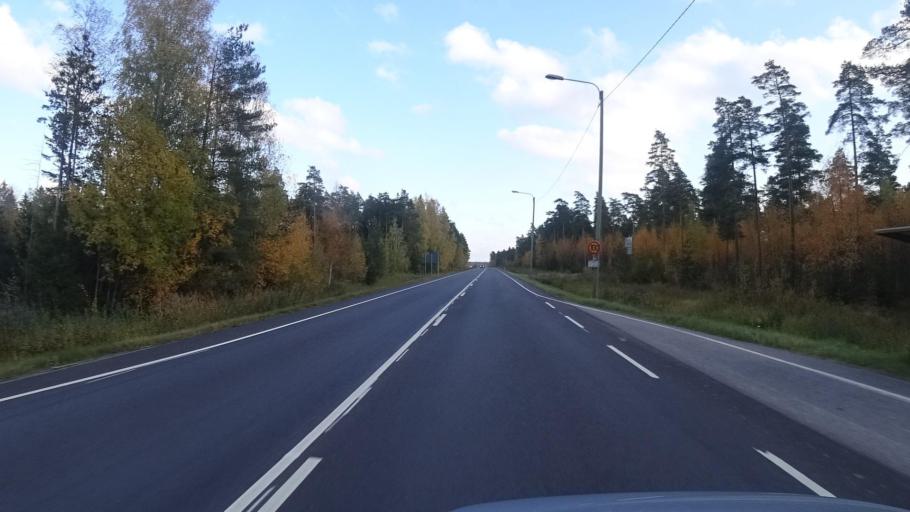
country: FI
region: Satakunta
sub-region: Rauma
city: Koeylioe
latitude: 61.0812
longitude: 22.2737
